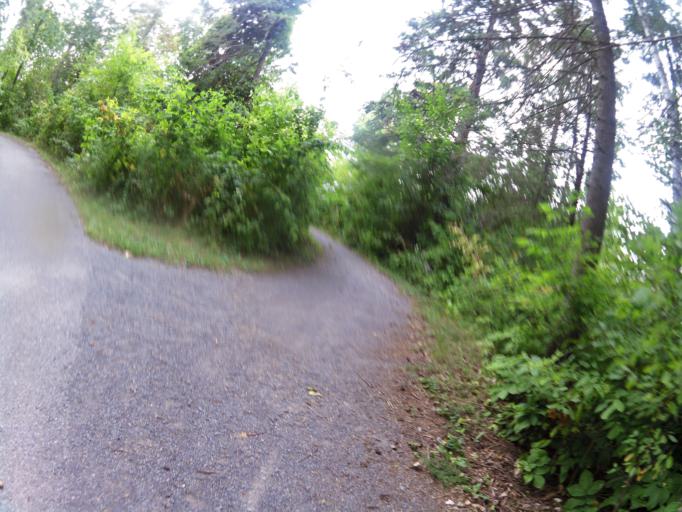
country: CA
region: Ontario
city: Bells Corners
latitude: 45.2776
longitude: -75.9324
